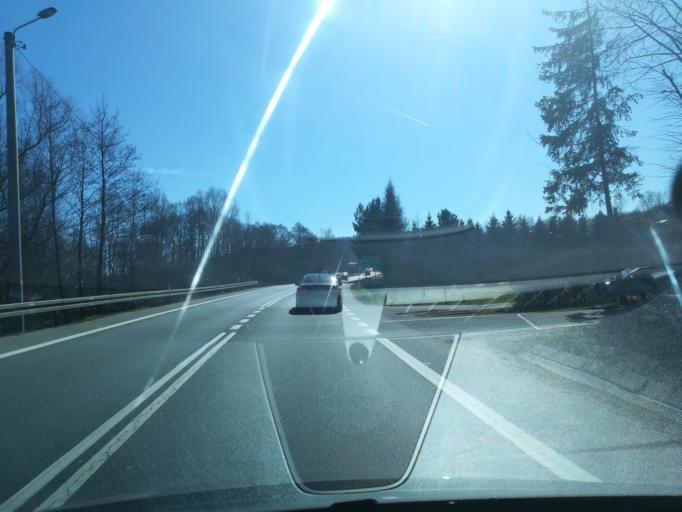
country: PL
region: Subcarpathian Voivodeship
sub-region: Powiat strzyzowski
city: Niebylec
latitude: 49.8627
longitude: 21.9030
